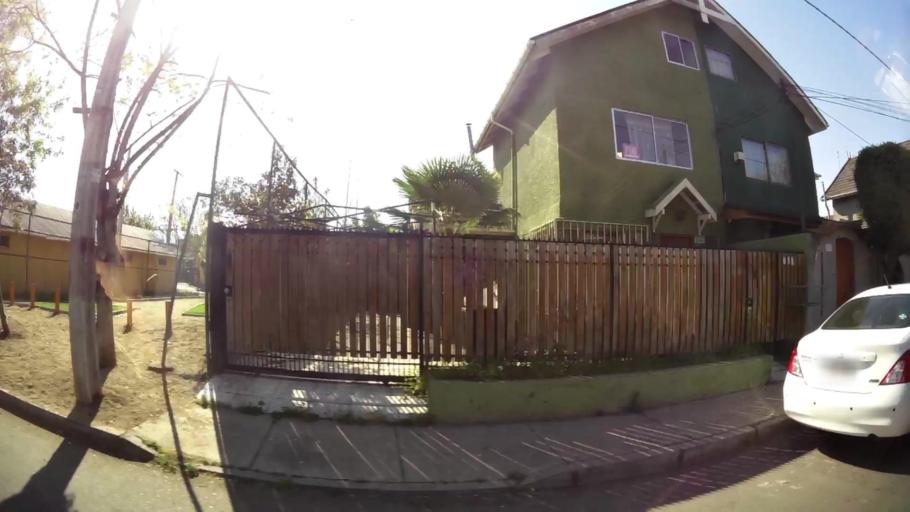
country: CL
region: Santiago Metropolitan
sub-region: Provincia de Santiago
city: Lo Prado
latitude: -33.4871
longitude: -70.7742
